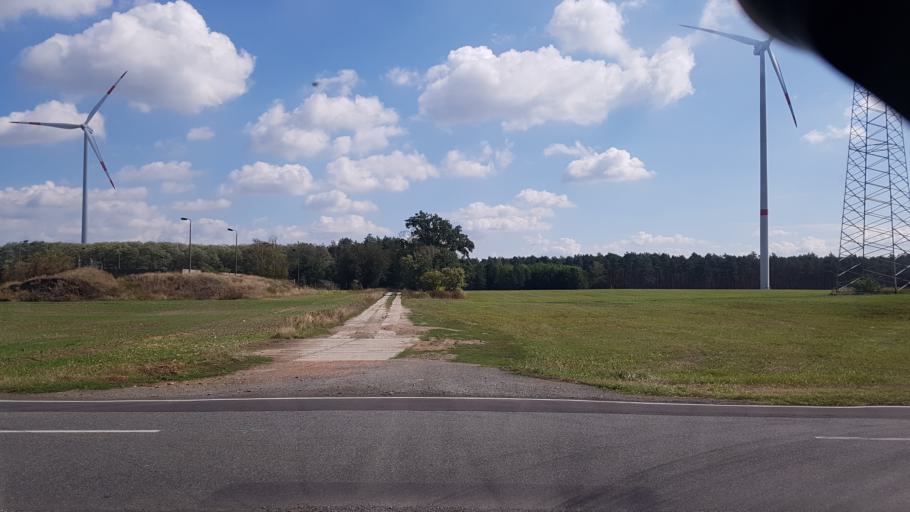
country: DE
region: Brandenburg
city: Drebkau
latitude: 51.6520
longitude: 14.2797
